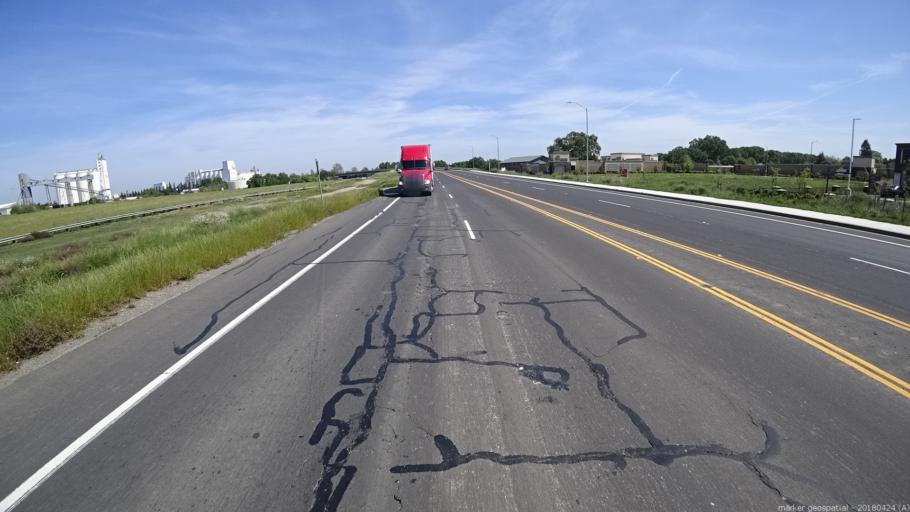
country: US
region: California
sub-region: Yolo County
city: West Sacramento
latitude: 38.5583
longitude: -121.5398
